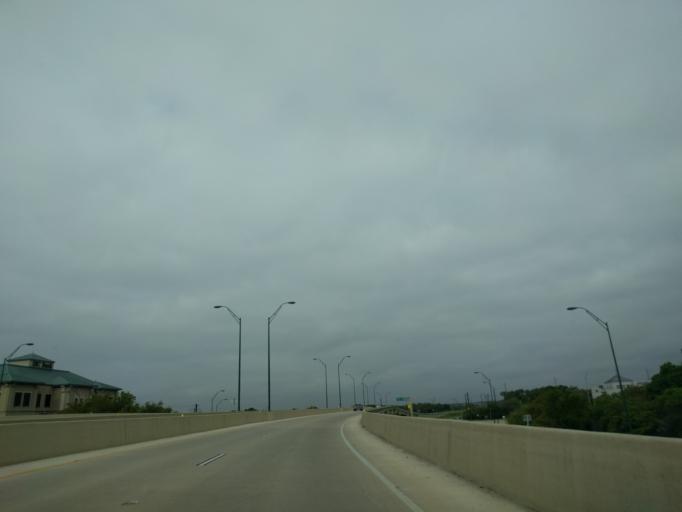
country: US
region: Texas
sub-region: Bexar County
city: Castle Hills
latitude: 29.5541
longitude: -98.4842
